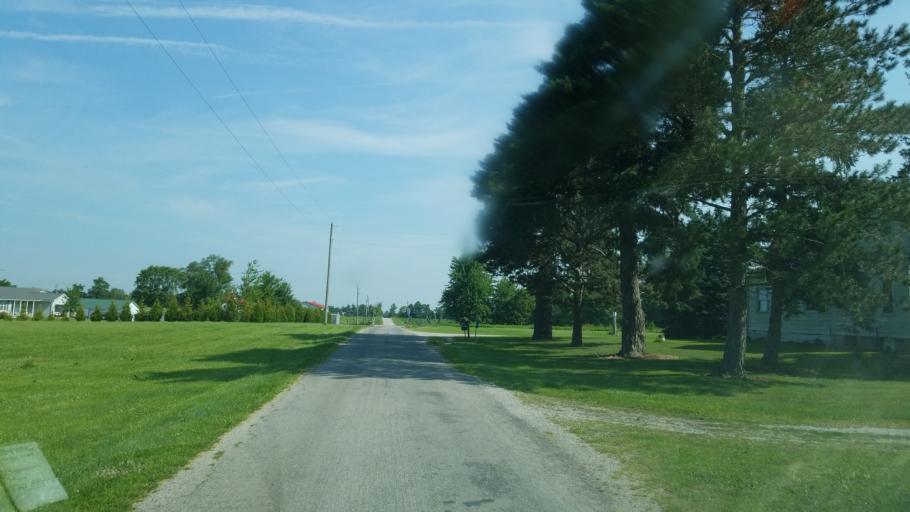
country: US
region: Ohio
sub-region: Sandusky County
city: Green Springs
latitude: 41.1082
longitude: -82.9960
